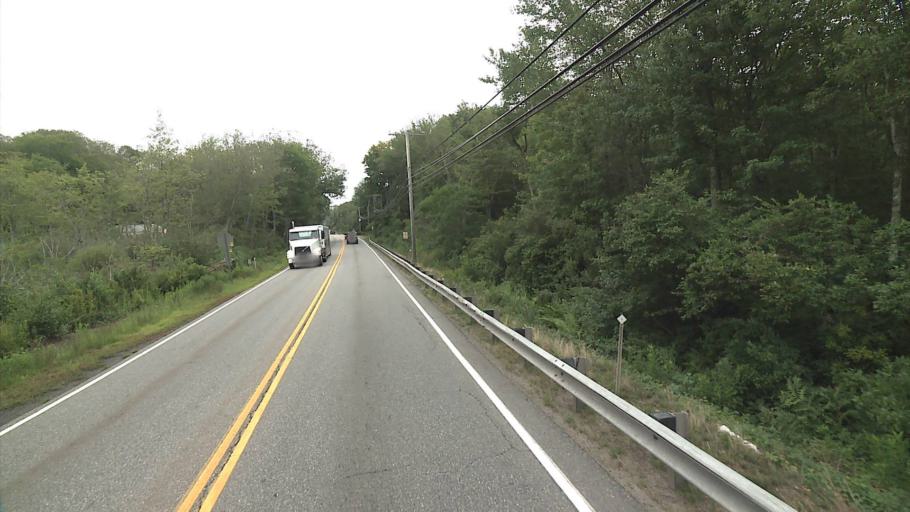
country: US
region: Connecticut
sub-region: New London County
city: Oxoboxo River
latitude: 41.4022
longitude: -72.1792
